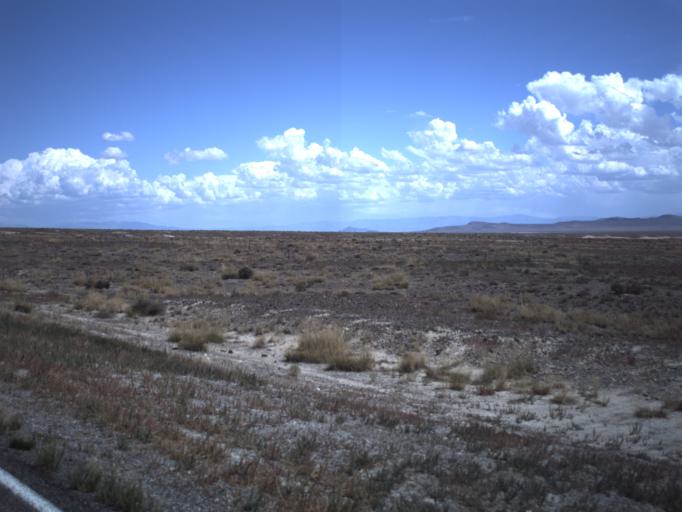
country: US
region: Utah
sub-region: Millard County
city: Delta
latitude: 39.1401
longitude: -113.0865
